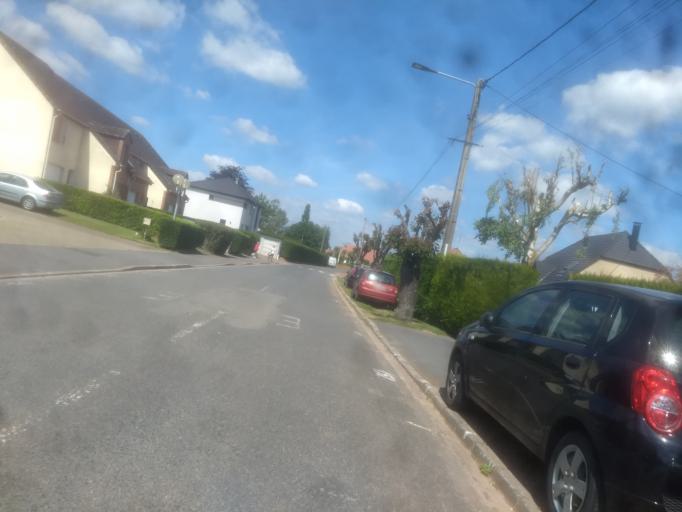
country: FR
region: Nord-Pas-de-Calais
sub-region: Departement du Pas-de-Calais
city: Agny
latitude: 50.2569
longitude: 2.7566
